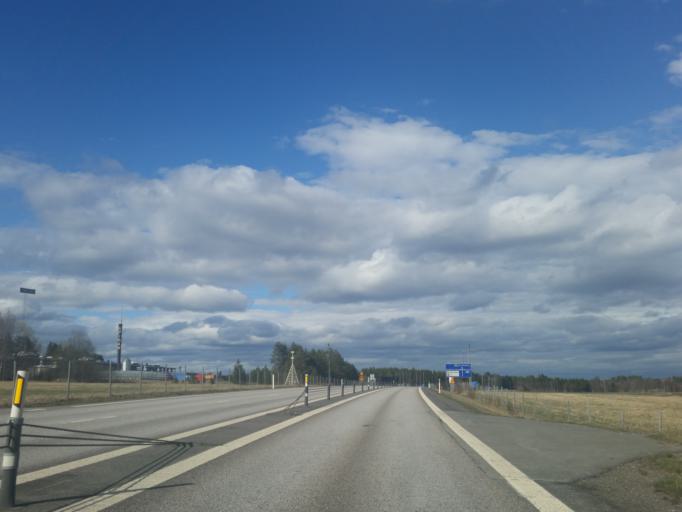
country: SE
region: Vaesterbotten
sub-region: Robertsfors Kommun
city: Robertsfors
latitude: 64.1645
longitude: 20.9206
